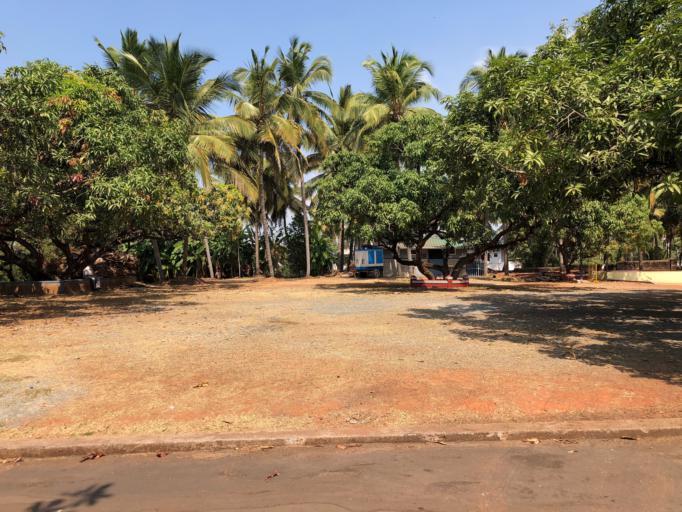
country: IN
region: Karnataka
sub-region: Dakshina Kannada
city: Mangalore
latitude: 12.8825
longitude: 74.8687
